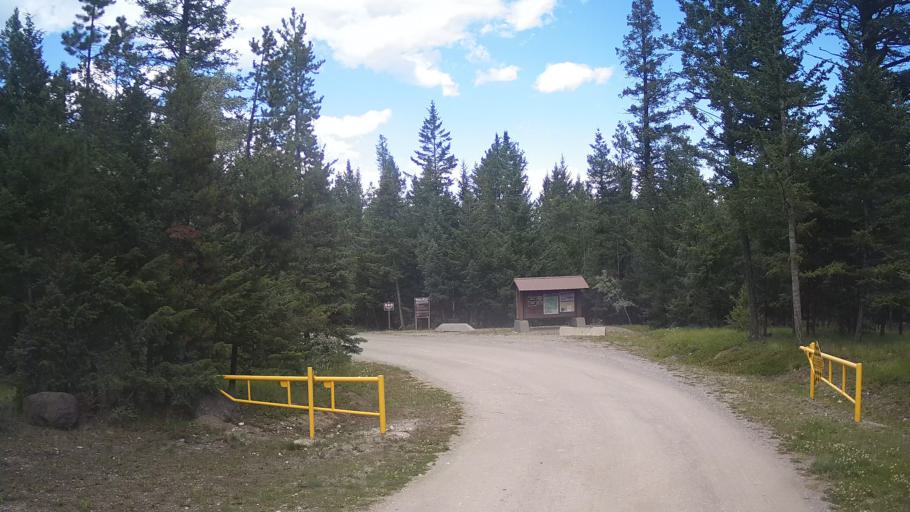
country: CA
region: British Columbia
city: Lillooet
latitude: 51.3090
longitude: -121.8235
